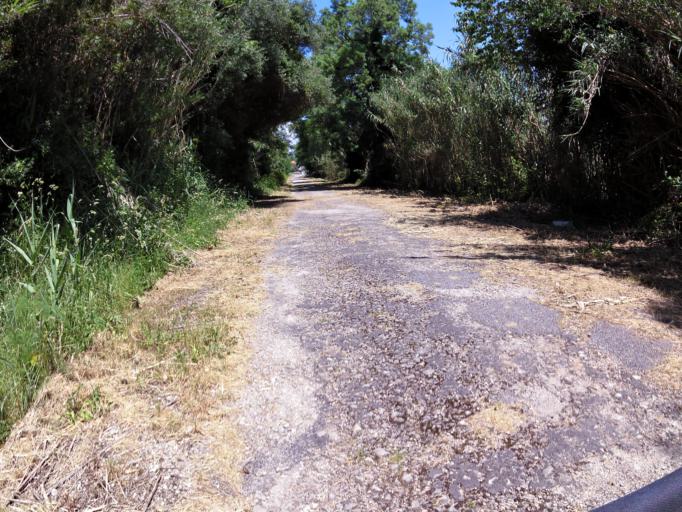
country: PT
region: Coimbra
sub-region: Montemor-O-Velho
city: Montemor-o-Velho
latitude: 40.1750
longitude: -8.6975
